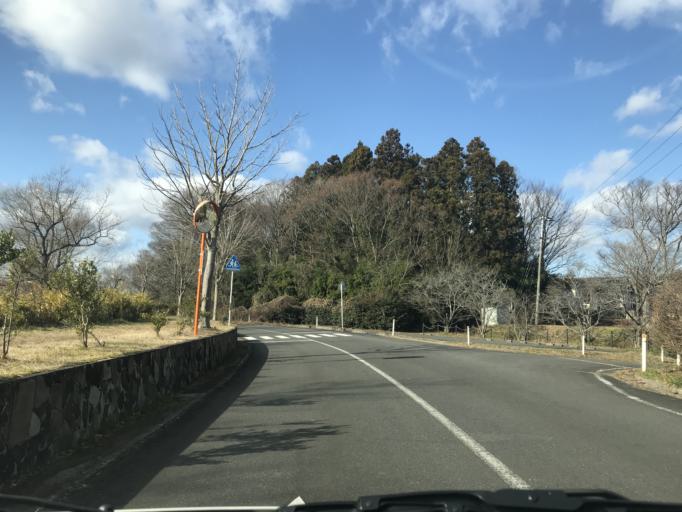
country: JP
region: Miyagi
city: Kogota
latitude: 38.7235
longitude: 141.0887
